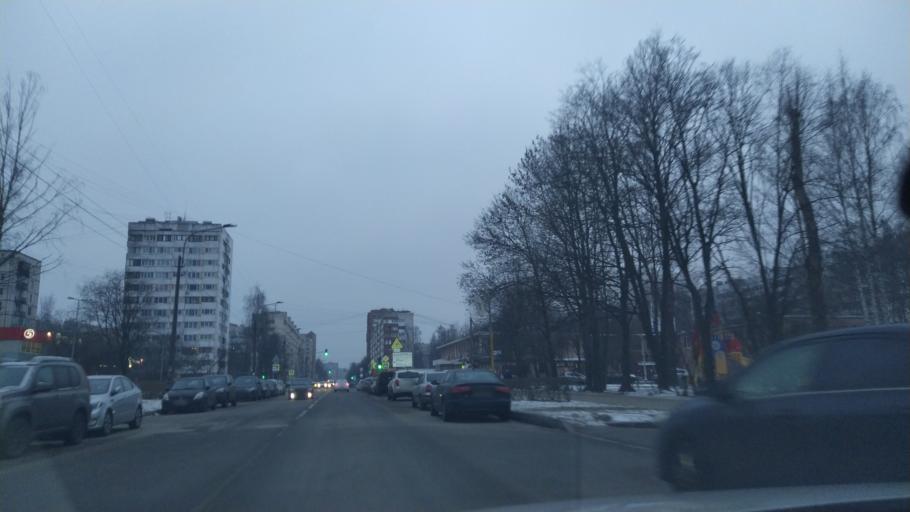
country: RU
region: St.-Petersburg
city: Grazhdanka
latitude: 60.0425
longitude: 30.4116
